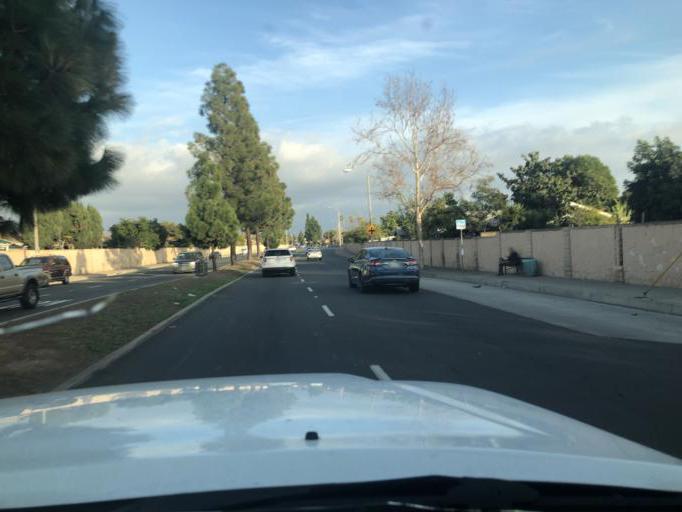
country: US
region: California
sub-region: Orange County
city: Santa Ana
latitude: 33.7271
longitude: -117.8634
